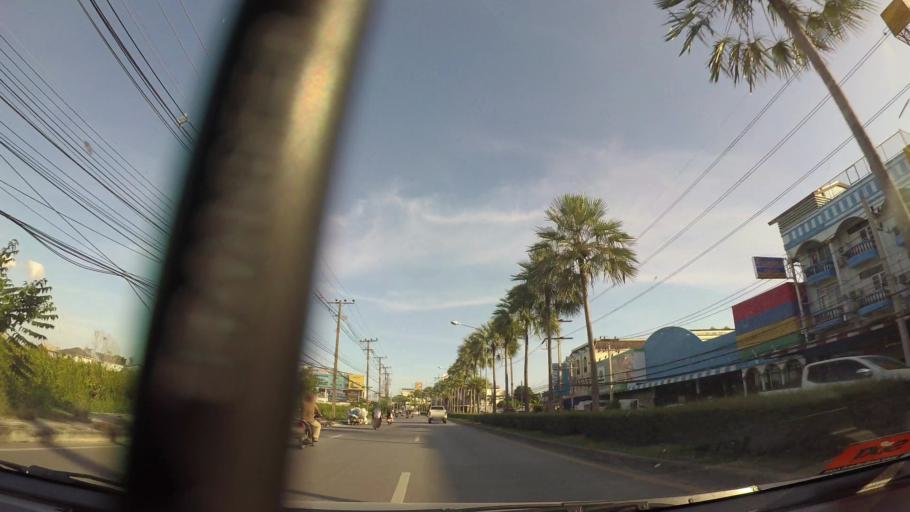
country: TH
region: Rayong
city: Rayong
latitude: 12.6938
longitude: 101.2732
